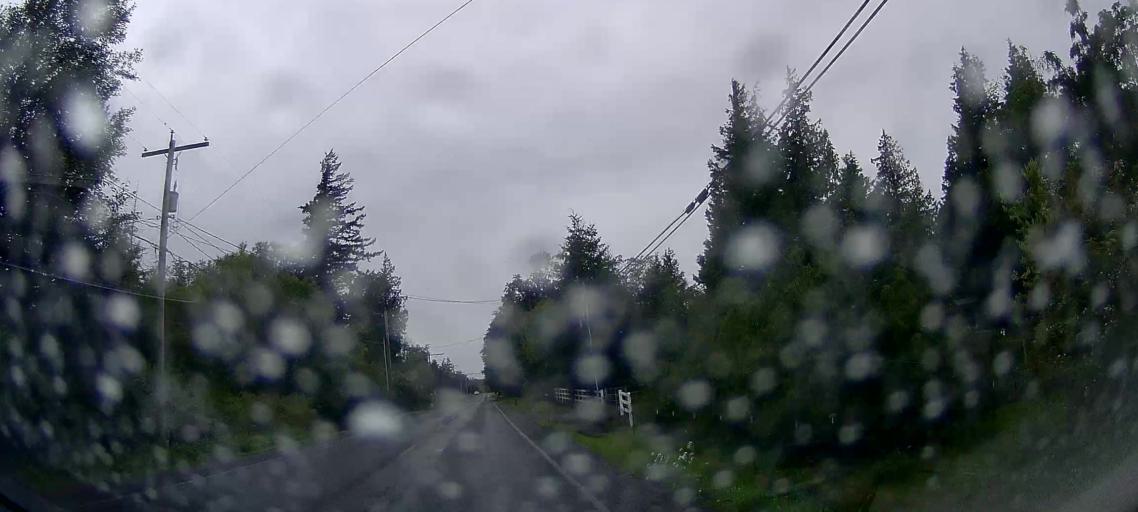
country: US
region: Washington
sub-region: Whatcom County
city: Marietta-Alderwood
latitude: 48.7832
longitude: -122.5595
